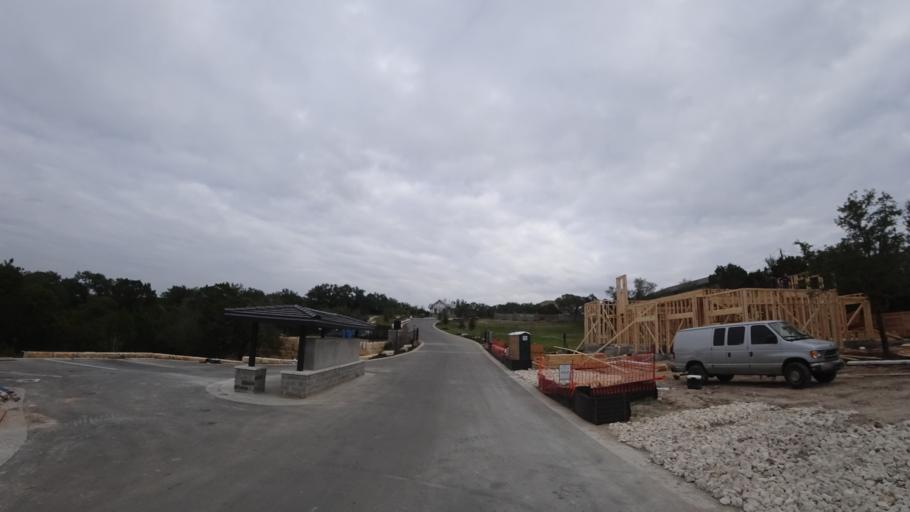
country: US
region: Texas
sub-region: Travis County
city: Bee Cave
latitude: 30.3128
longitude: -97.9137
